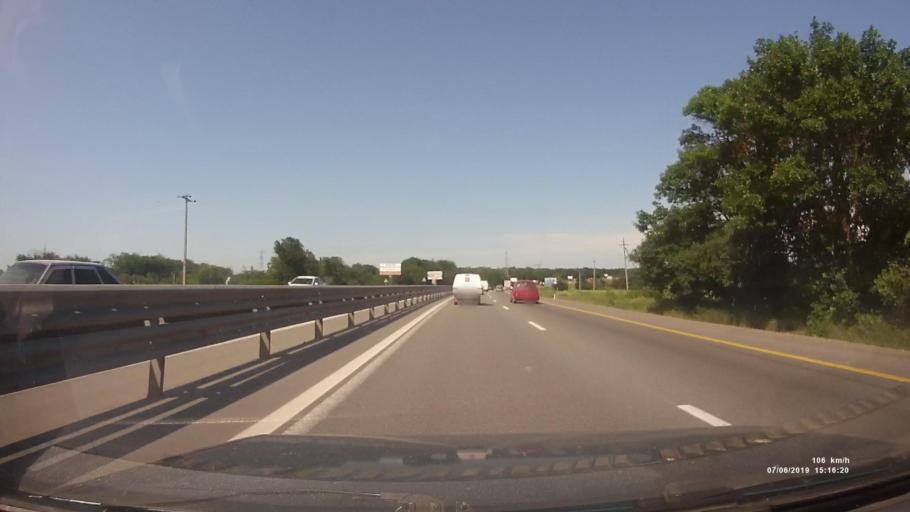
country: RU
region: Rostov
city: Grushevskaya
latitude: 47.3906
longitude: 39.9175
